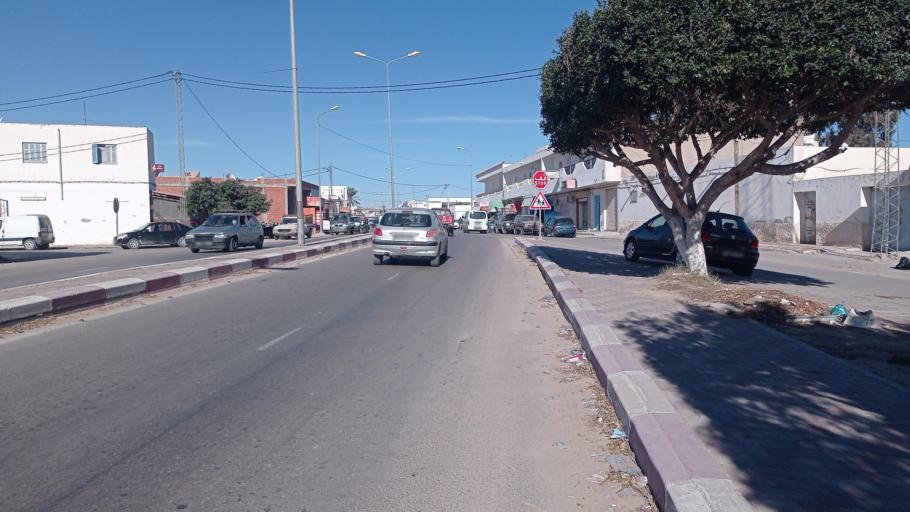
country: TN
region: Qabis
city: Gabes
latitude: 33.8389
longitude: 10.1160
